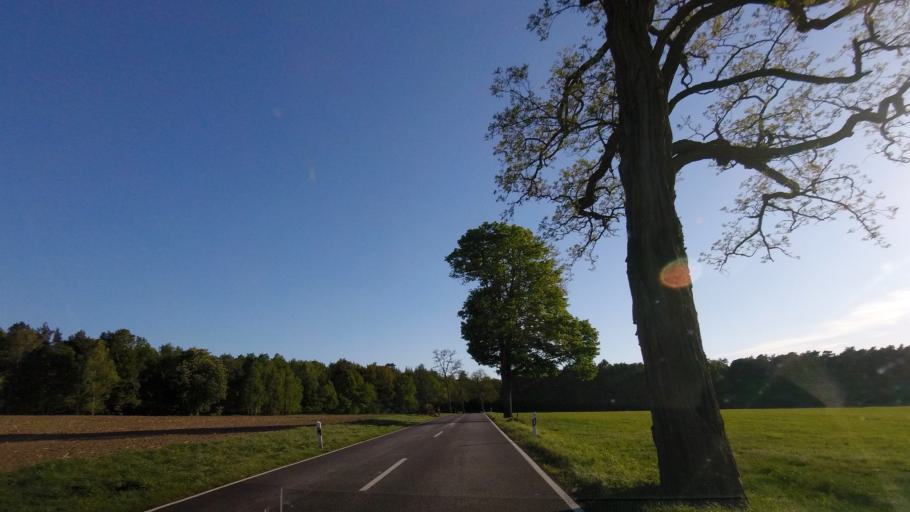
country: DE
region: Brandenburg
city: Baruth
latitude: 52.0081
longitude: 13.4445
